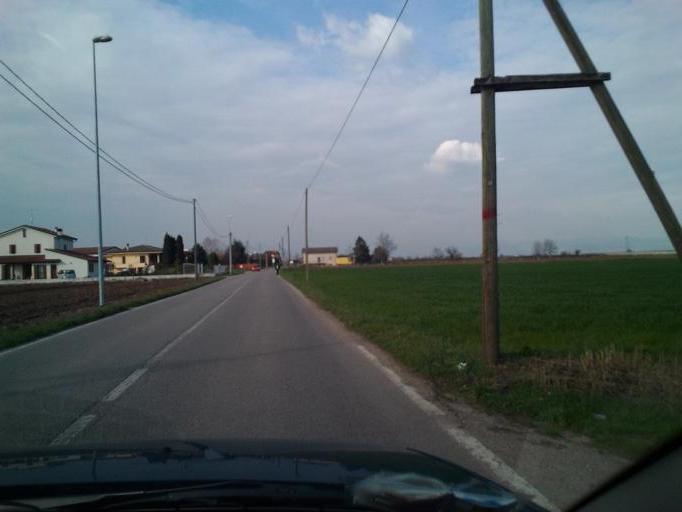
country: IT
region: Veneto
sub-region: Provincia di Verona
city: Villafranca di Verona
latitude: 45.3736
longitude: 10.8631
